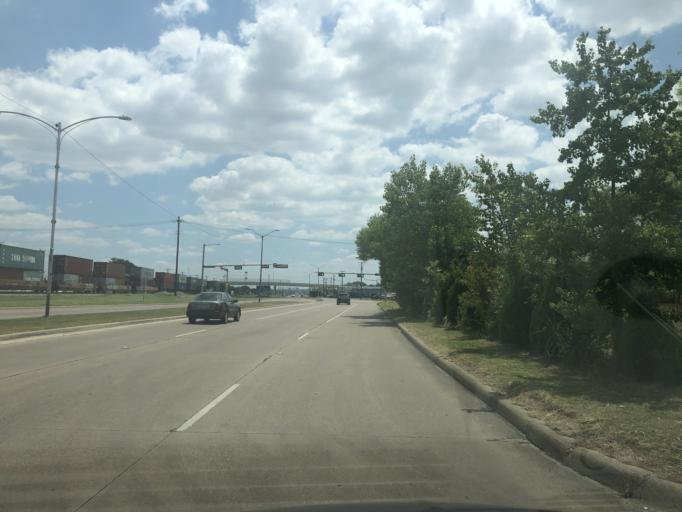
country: US
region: Texas
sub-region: Dallas County
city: Grand Prairie
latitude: 32.7446
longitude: -96.9994
